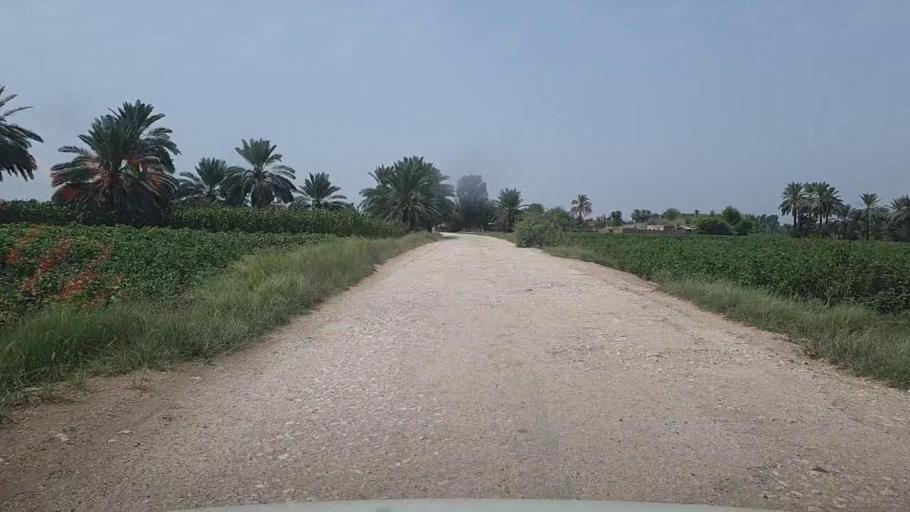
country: PK
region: Sindh
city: Pano Aqil
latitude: 27.8515
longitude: 69.1401
